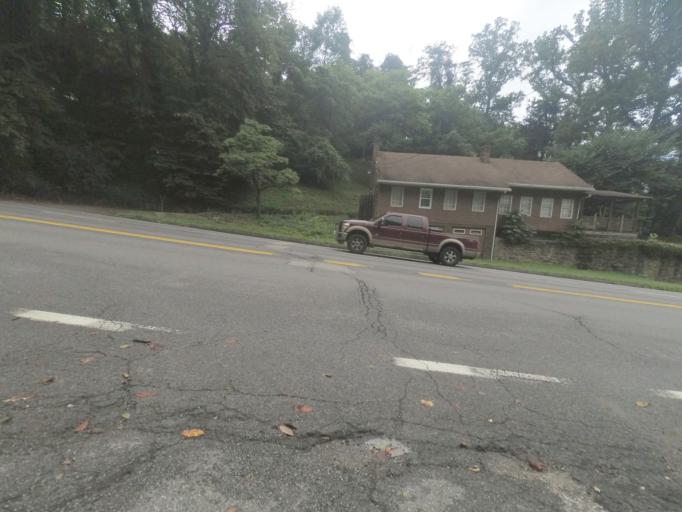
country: US
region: West Virginia
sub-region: Cabell County
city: Huntington
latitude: 38.4048
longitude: -82.4476
